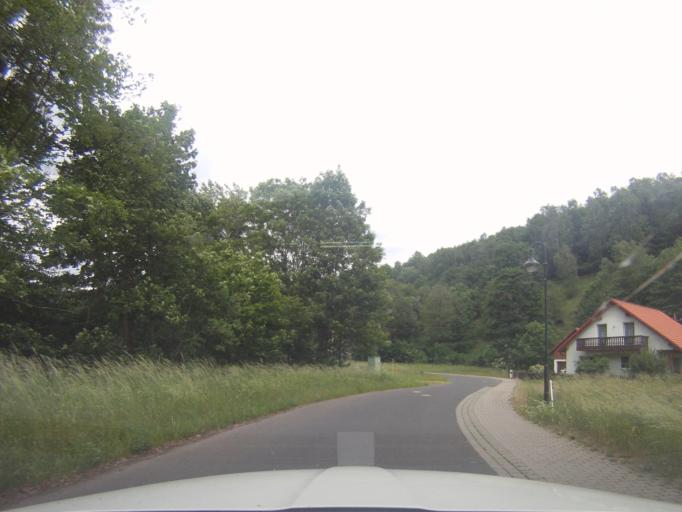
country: DE
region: Thuringia
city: Frauenwald
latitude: 50.5267
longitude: 10.8796
